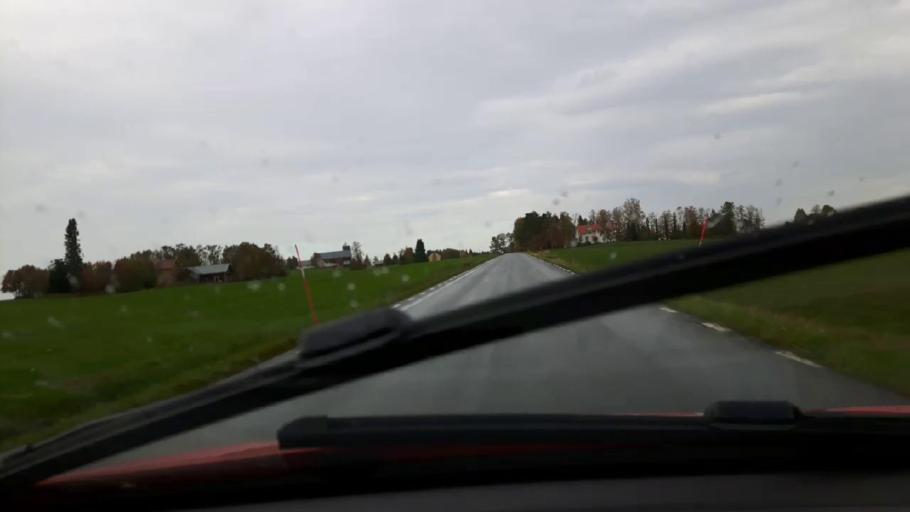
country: SE
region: Jaemtland
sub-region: Bergs Kommun
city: Hoverberg
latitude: 63.0320
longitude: 14.3451
